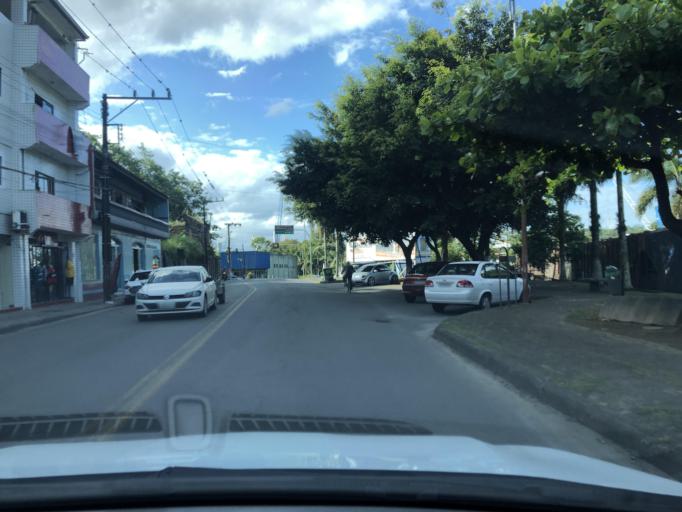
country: BR
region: Santa Catarina
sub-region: Sao Francisco Do Sul
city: Sao Francisco do Sul
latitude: -26.2430
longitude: -48.6353
